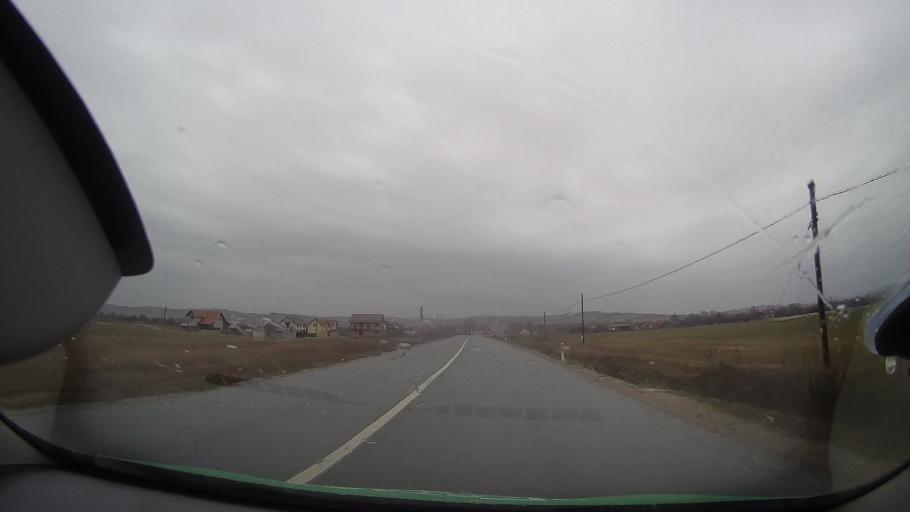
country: RO
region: Bihor
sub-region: Comuna Pocola
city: Pocola
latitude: 46.6908
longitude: 22.2980
